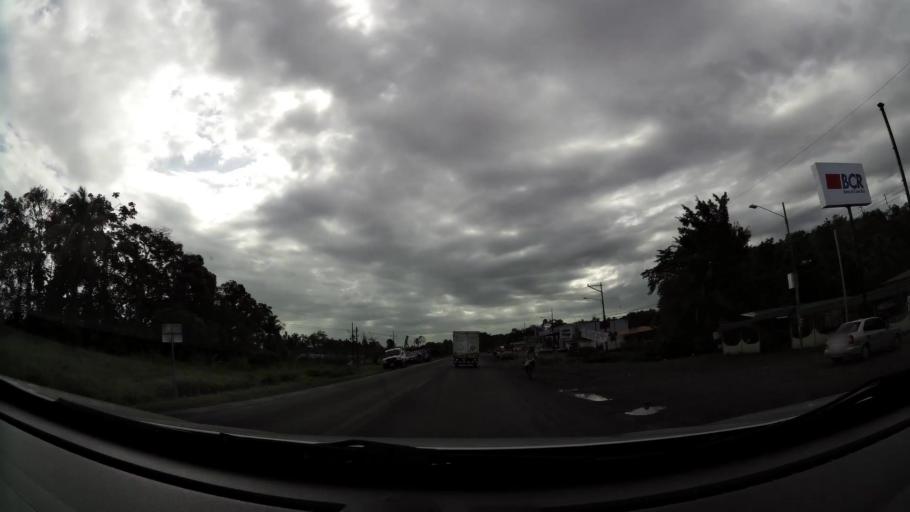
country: CR
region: Limon
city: Pocora
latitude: 10.1685
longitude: -83.6061
